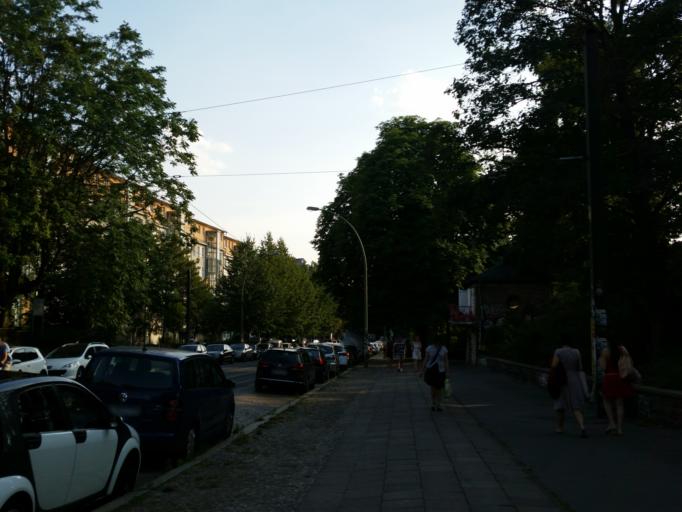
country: DE
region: Berlin
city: Berlin
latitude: 52.5328
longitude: 13.4039
